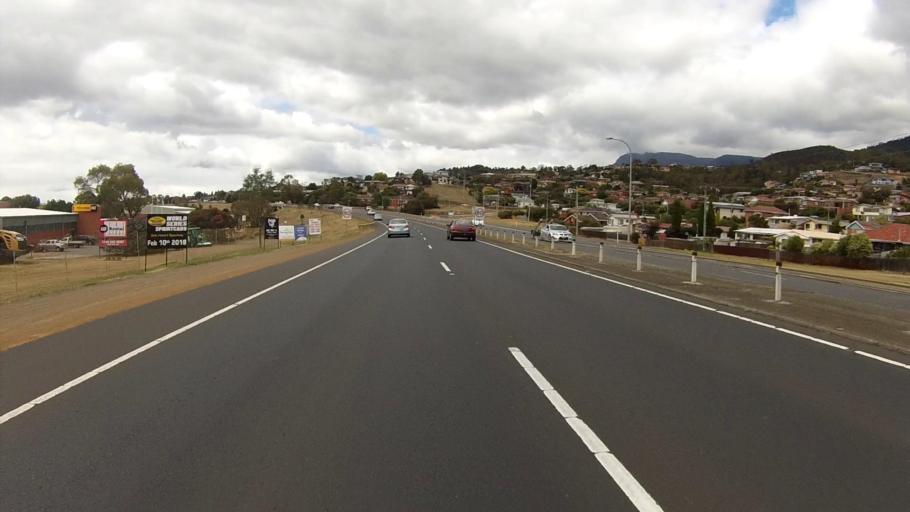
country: AU
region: Tasmania
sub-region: Glenorchy
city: Berriedale
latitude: -42.8129
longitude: 147.2510
